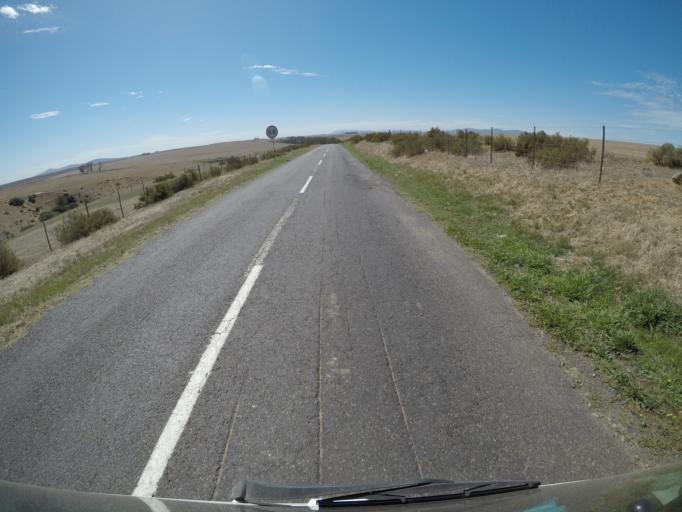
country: ZA
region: Western Cape
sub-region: City of Cape Town
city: Atlantis
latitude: -33.6823
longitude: 18.6018
